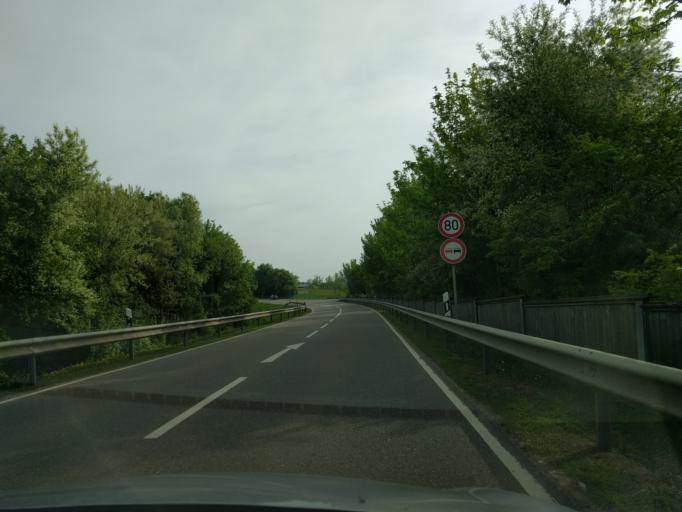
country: DE
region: Bavaria
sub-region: Upper Palatinate
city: Wiesent
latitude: 49.0136
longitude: 12.3714
